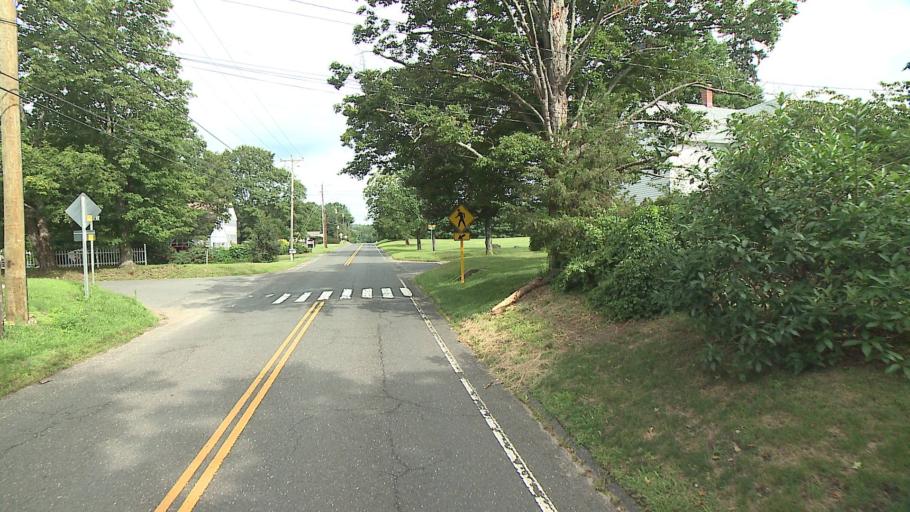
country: US
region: Connecticut
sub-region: Litchfield County
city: Woodbury
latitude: 41.5540
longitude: -73.2081
